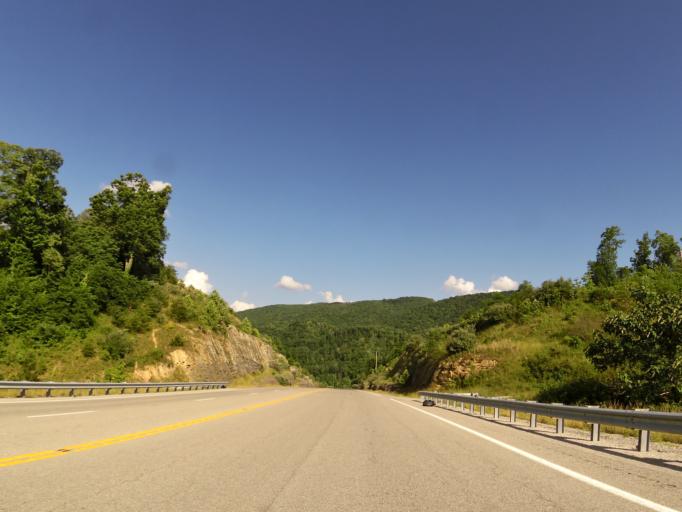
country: US
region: Virginia
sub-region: Lee County
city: Jonesville
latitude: 36.7625
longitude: -83.1995
